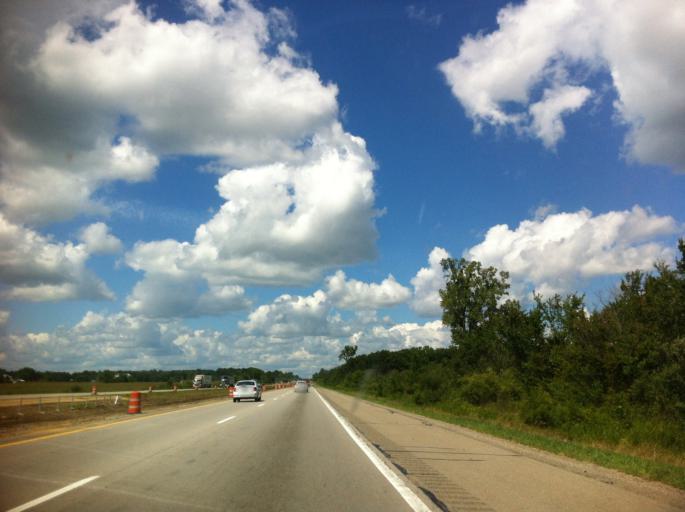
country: US
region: Michigan
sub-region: Washtenaw County
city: Milan
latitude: 42.1226
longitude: -83.6824
